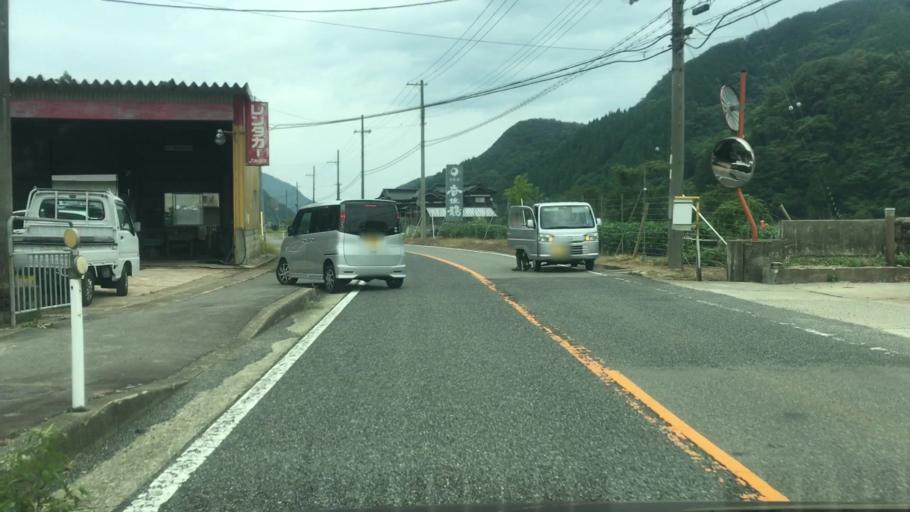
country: JP
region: Hyogo
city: Toyooka
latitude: 35.6303
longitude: 134.6797
